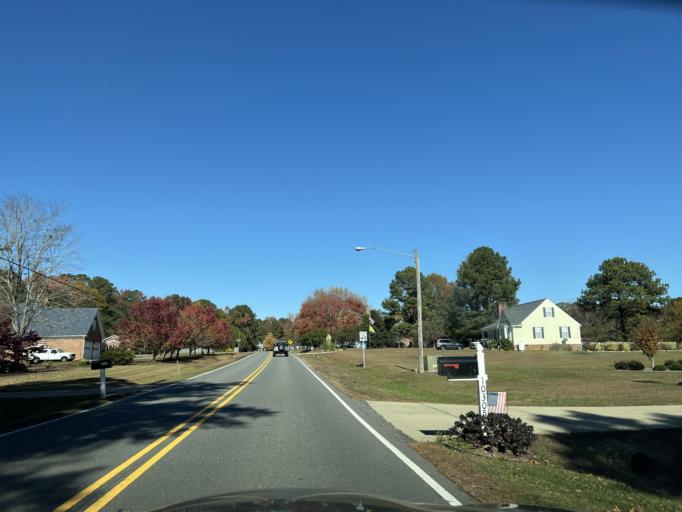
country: US
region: North Carolina
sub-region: Wake County
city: Fuquay-Varina
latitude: 35.6226
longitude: -78.7316
